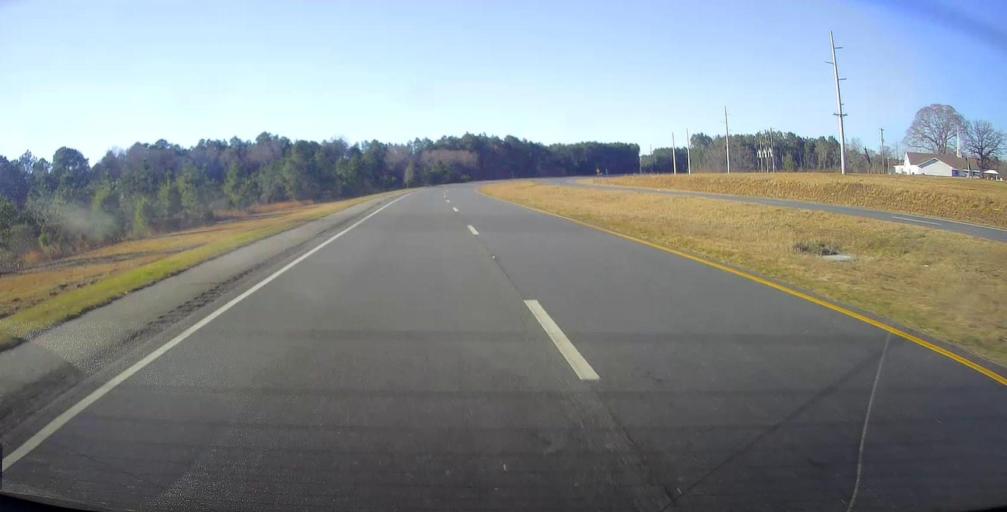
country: US
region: Georgia
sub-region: Lee County
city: Leesburg
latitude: 31.8134
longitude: -84.2121
